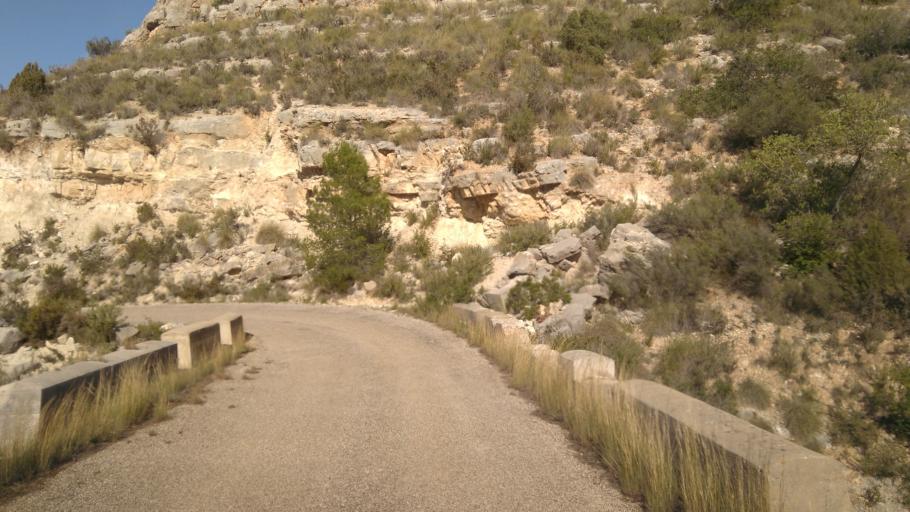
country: ES
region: Valencia
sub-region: Provincia de Valencia
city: Sumacarcer
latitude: 39.1536
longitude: -0.6498
